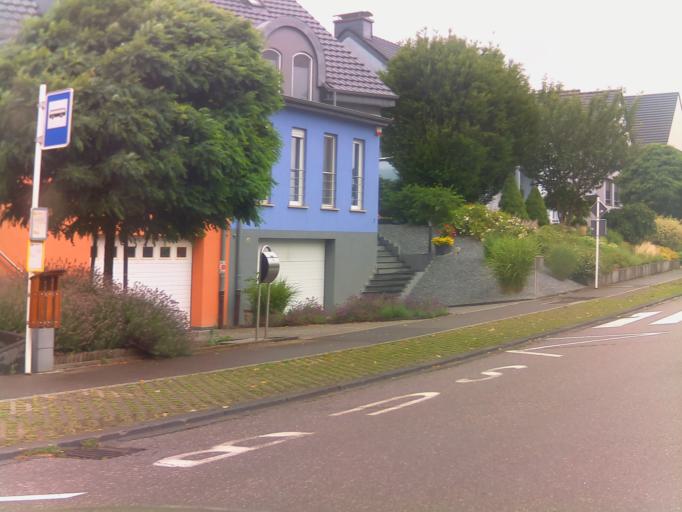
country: LU
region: Grevenmacher
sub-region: Canton de Remich
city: Mondorf-les-Bains
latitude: 49.4874
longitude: 6.3199
